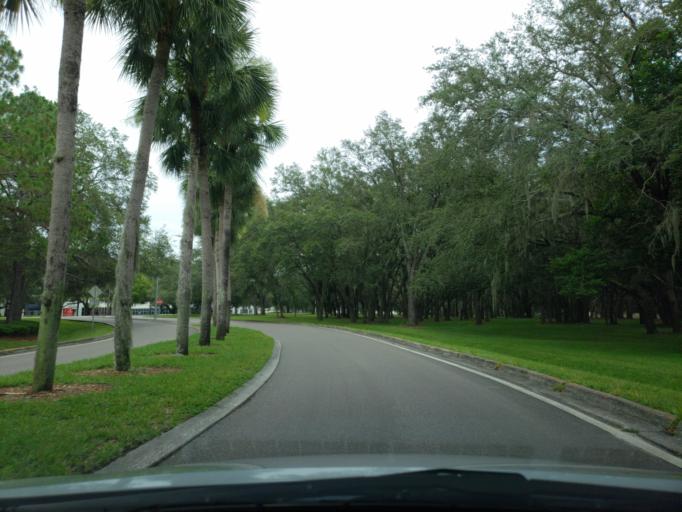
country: US
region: Florida
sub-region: Hillsborough County
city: Temple Terrace
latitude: 28.0628
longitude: -82.3727
